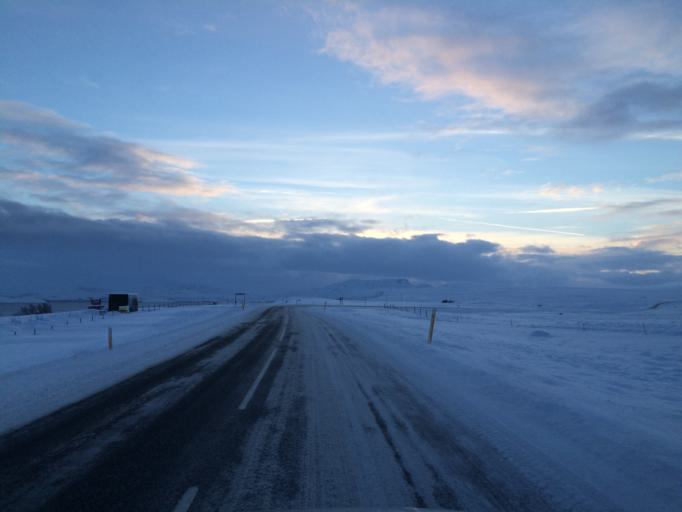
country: IS
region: South
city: Hveragerdi
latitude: 64.2325
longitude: -21.1977
